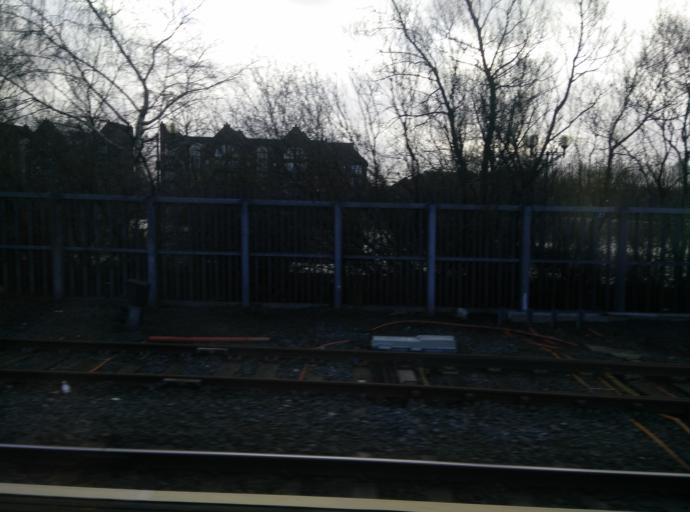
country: GB
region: Northern Ireland
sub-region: City of Belfast
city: Belfast
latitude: 54.5929
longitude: -5.9183
